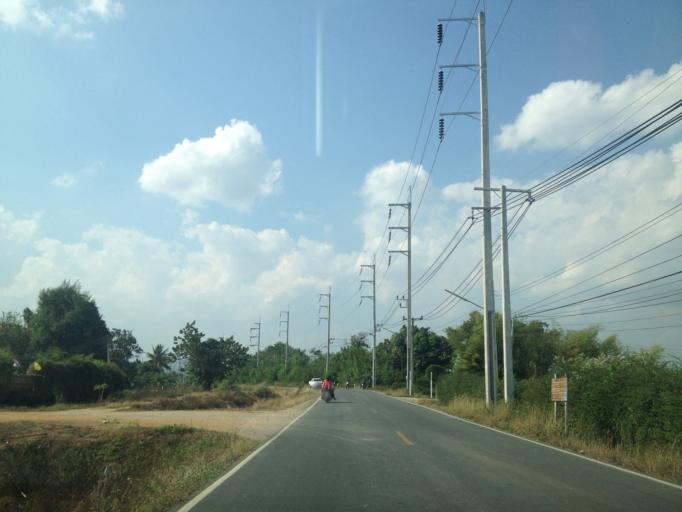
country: TH
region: Chiang Mai
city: Hang Dong
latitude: 18.6743
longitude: 98.9120
